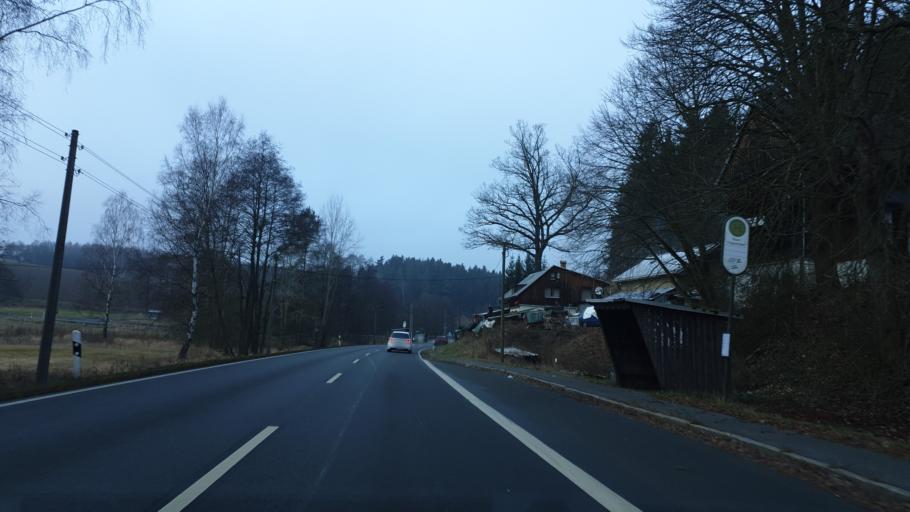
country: DE
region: Saxony
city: Bad Brambach
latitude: 50.2580
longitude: 12.3018
